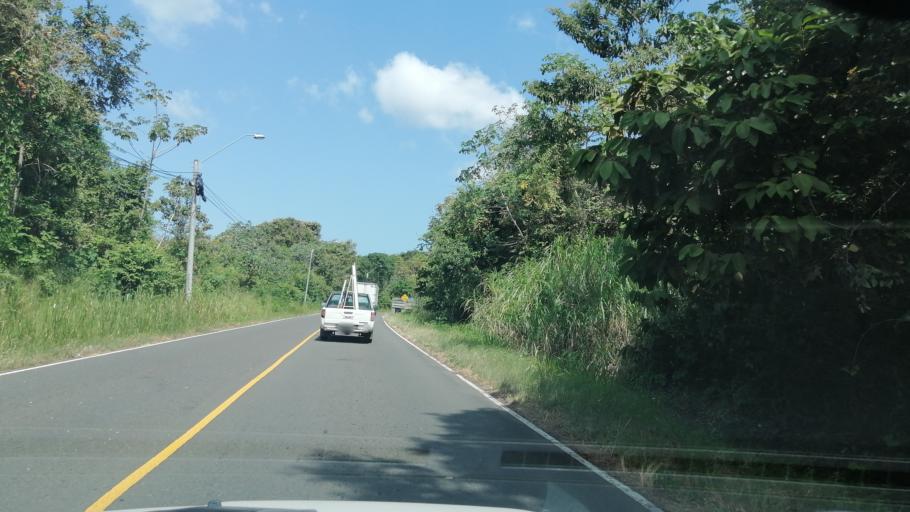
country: PA
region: Panama
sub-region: Distrito de Panama
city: Ancon
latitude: 8.9309
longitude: -79.5746
